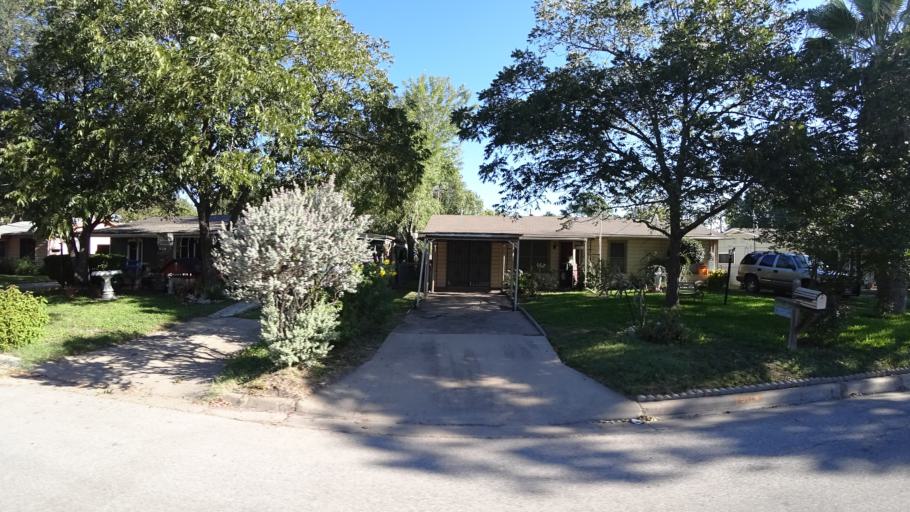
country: US
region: Texas
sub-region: Travis County
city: Austin
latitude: 30.2349
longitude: -97.7004
